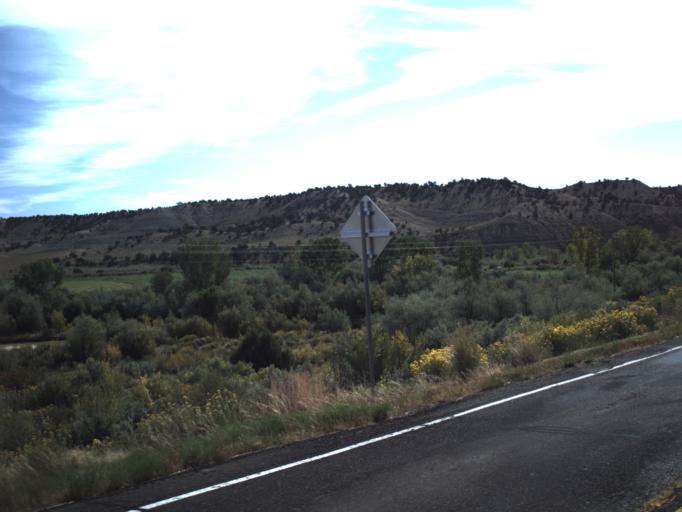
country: US
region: Utah
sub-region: Garfield County
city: Panguitch
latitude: 37.6108
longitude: -112.0625
